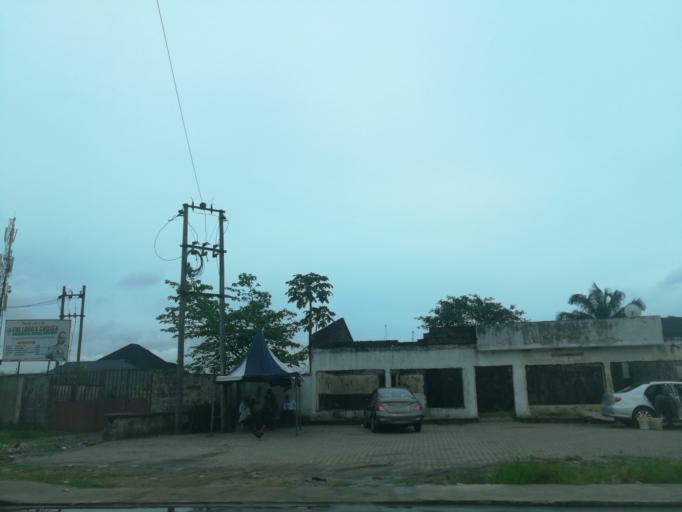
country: NG
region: Rivers
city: Port Harcourt
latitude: 4.8158
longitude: 6.9951
